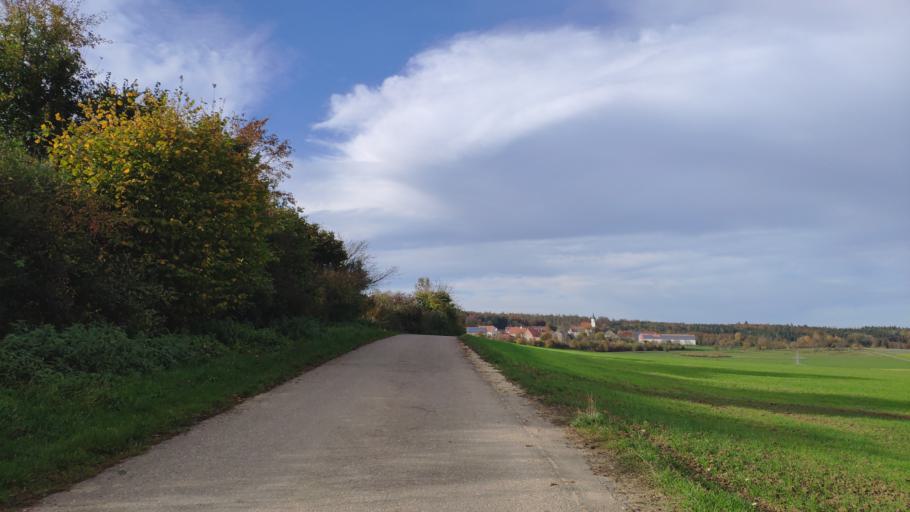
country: DE
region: Baden-Wuerttemberg
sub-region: Tuebingen Region
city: Erbach
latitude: 48.3830
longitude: 9.9187
